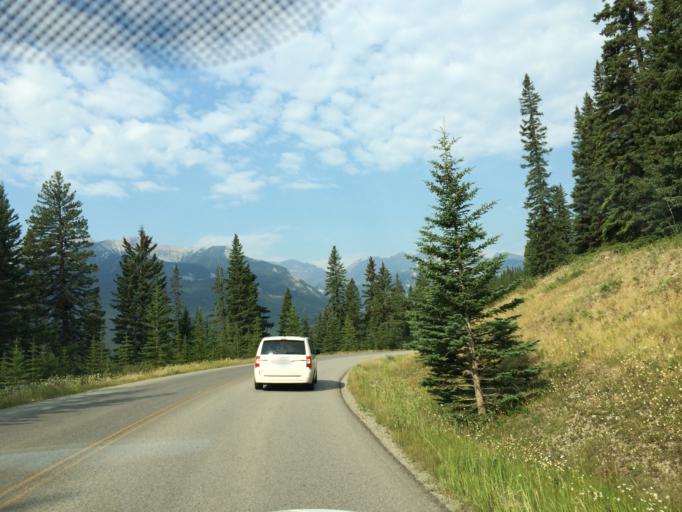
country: CA
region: Alberta
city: Banff
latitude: 51.1686
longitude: -115.6838
